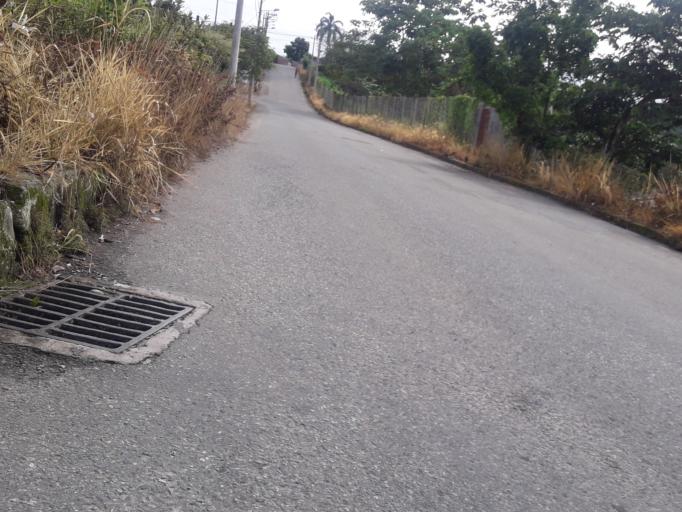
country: EC
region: Napo
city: Tena
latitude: -0.9889
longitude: -77.8124
